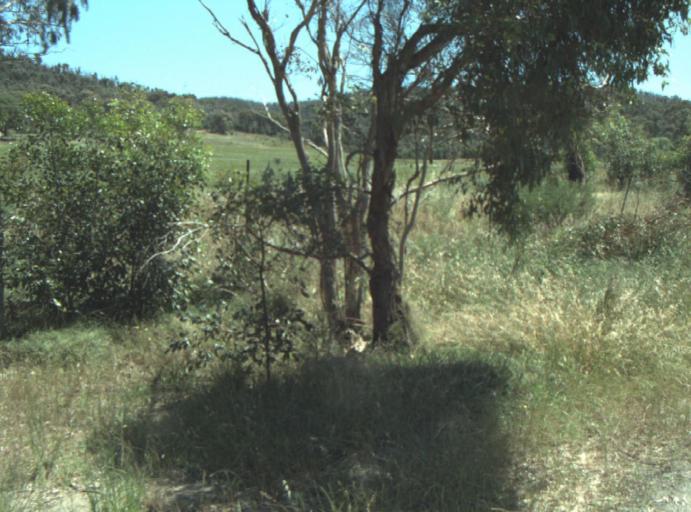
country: AU
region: Victoria
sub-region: Greater Geelong
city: Lara
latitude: -37.8475
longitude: 144.2821
